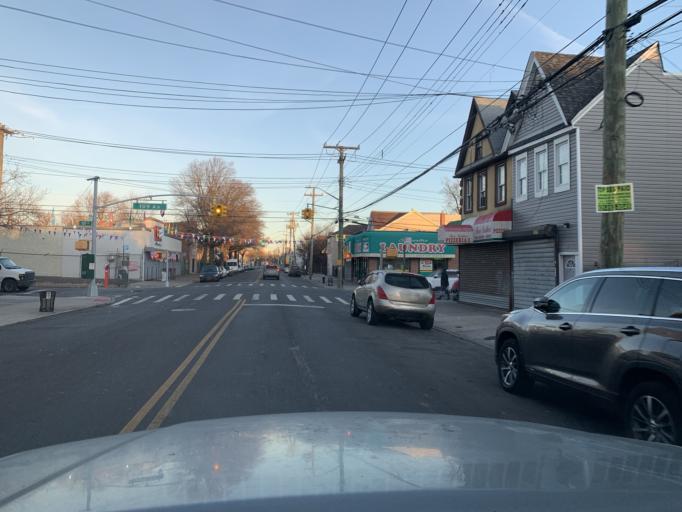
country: US
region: New York
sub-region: Queens County
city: Jamaica
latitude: 40.6948
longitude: -73.7899
